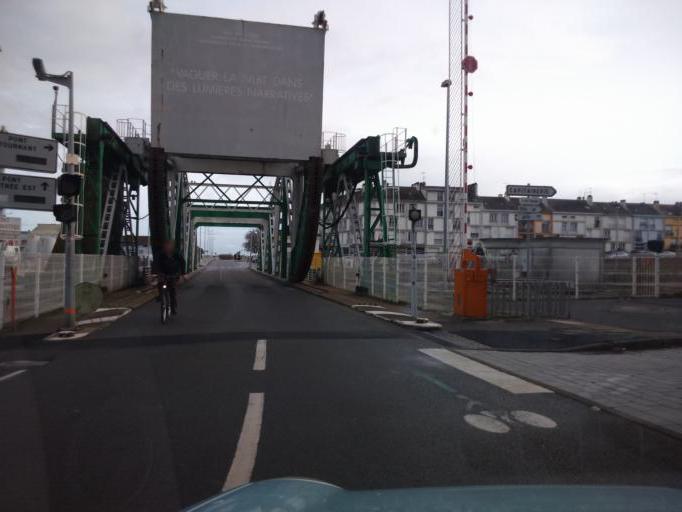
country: FR
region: Pays de la Loire
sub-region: Departement de la Loire-Atlantique
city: Saint-Nazaire
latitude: 47.2728
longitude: -2.2023
